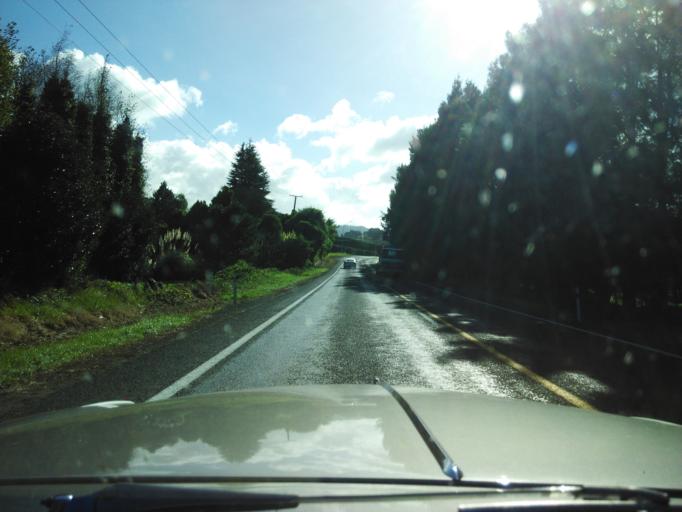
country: NZ
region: Bay of Plenty
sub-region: Western Bay of Plenty District
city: Katikati
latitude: -37.5391
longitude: 175.9121
